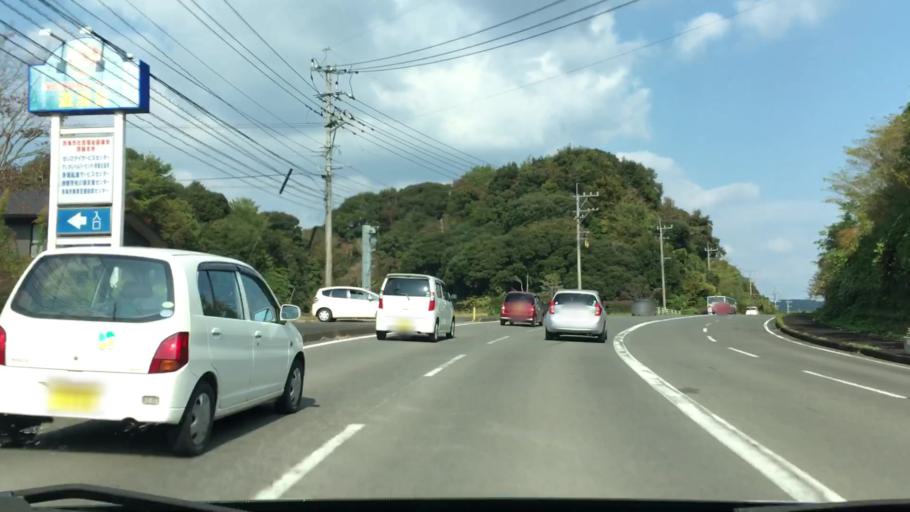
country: JP
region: Nagasaki
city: Sasebo
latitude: 32.9905
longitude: 129.7492
